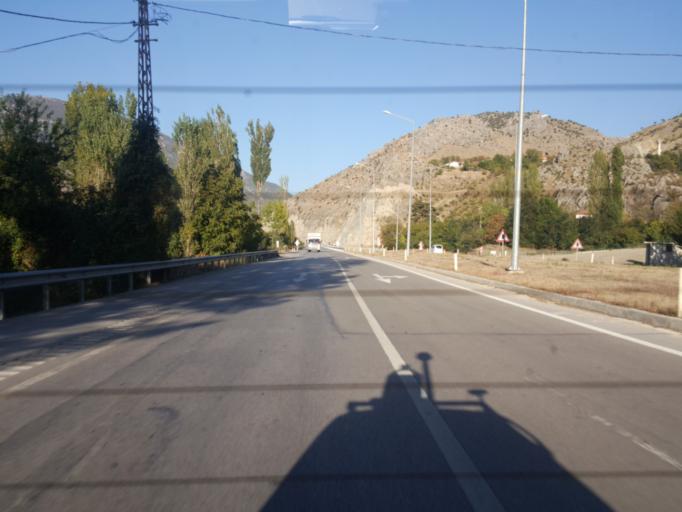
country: TR
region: Amasya
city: Amasya
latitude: 40.6773
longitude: 35.8759
